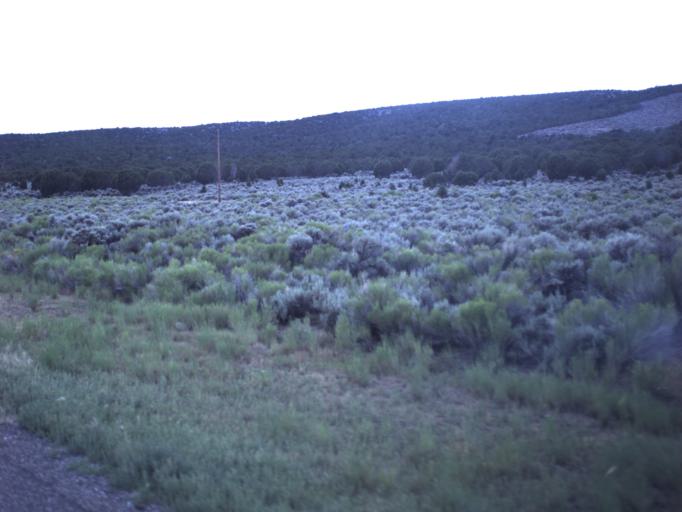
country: US
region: Utah
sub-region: Sevier County
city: Monroe
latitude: 38.6017
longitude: -111.8466
